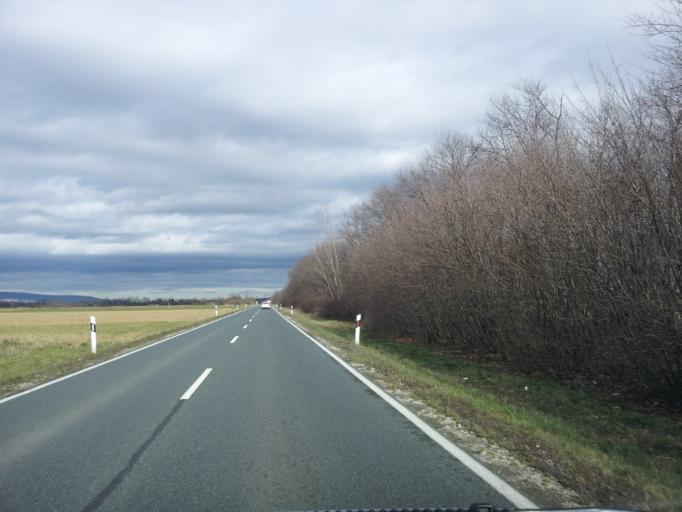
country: HU
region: Vas
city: Gencsapati
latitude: 47.2983
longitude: 16.6064
